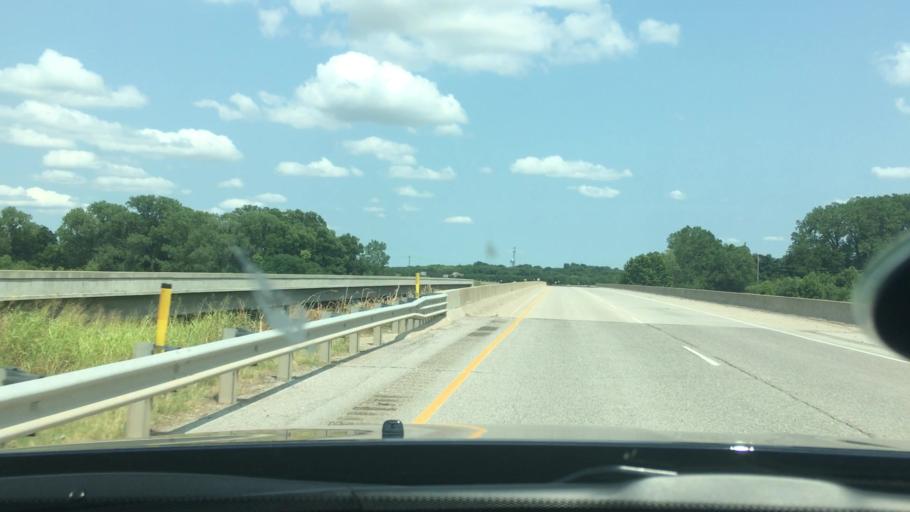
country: US
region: Oklahoma
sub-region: Murray County
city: Davis
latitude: 34.5045
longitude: -97.1435
